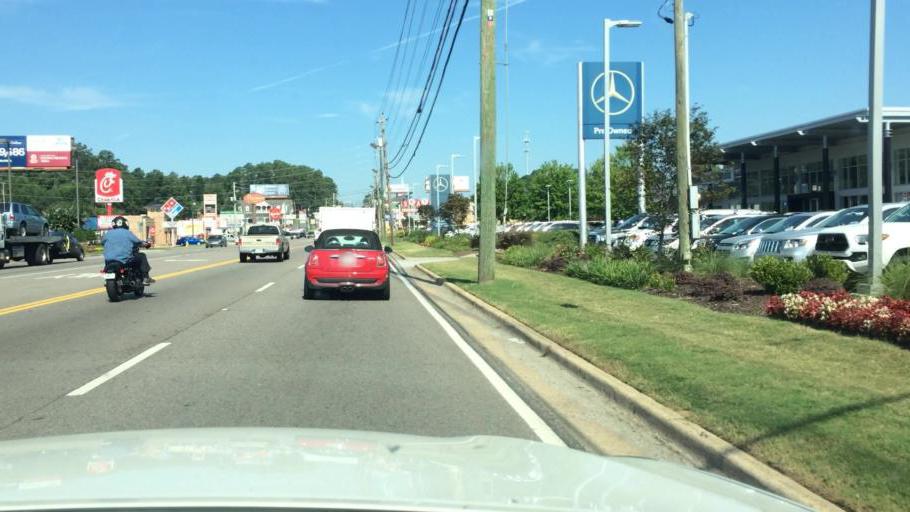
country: US
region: Georgia
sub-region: Columbia County
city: Martinez
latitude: 33.5133
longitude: -82.0509
